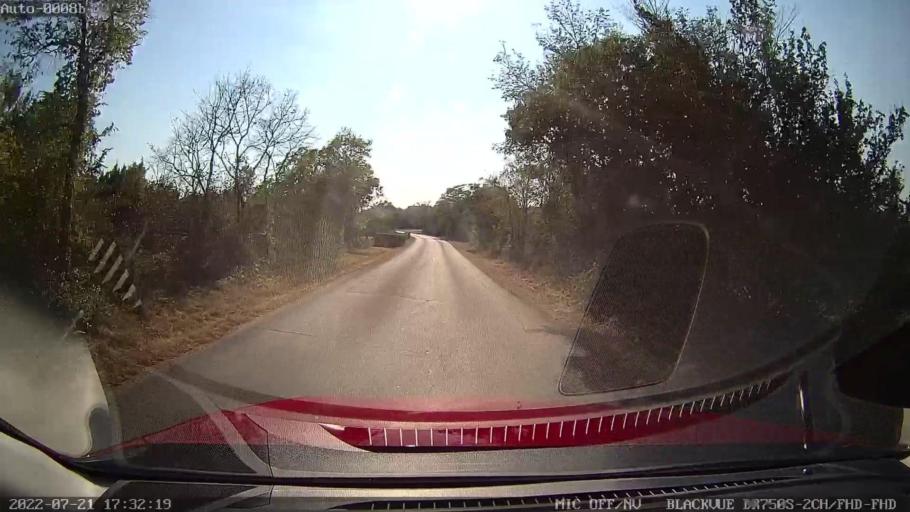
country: HR
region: Istarska
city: Karojba
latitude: 45.1747
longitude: 13.7547
